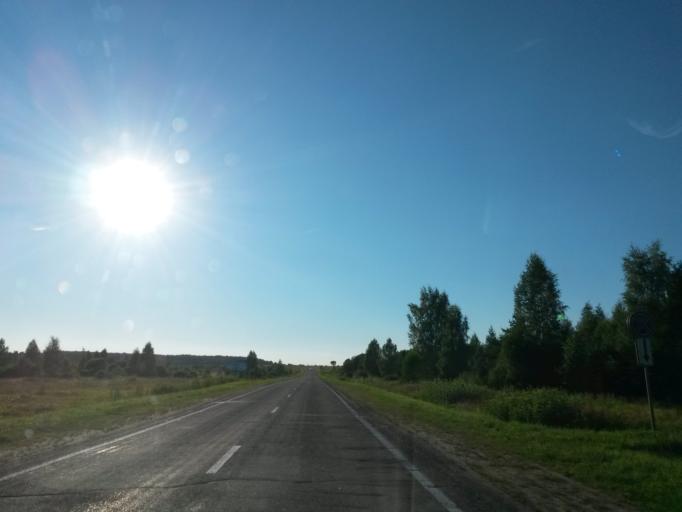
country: RU
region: Jaroslavl
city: Gavrilov-Yam
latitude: 57.2801
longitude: 39.9132
